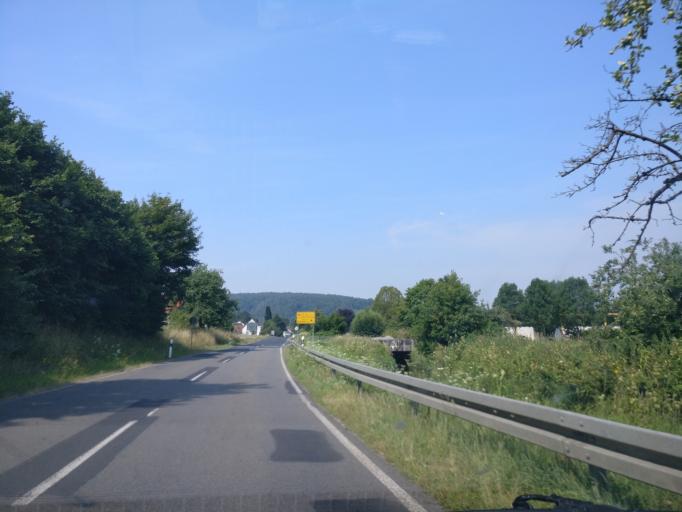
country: DE
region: Lower Saxony
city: Bodenfelde
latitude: 51.6231
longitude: 9.5686
